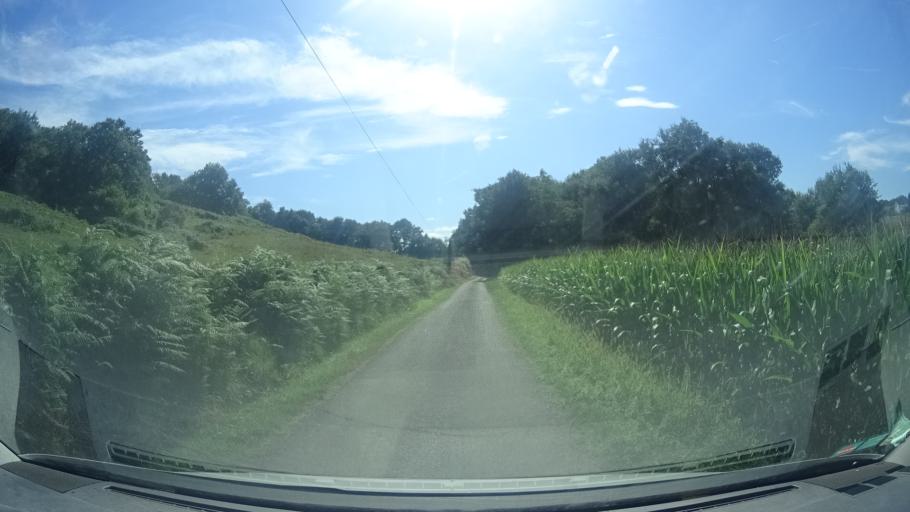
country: FR
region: Aquitaine
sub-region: Departement des Pyrenees-Atlantiques
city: Orthez
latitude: 43.4998
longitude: -0.6988
